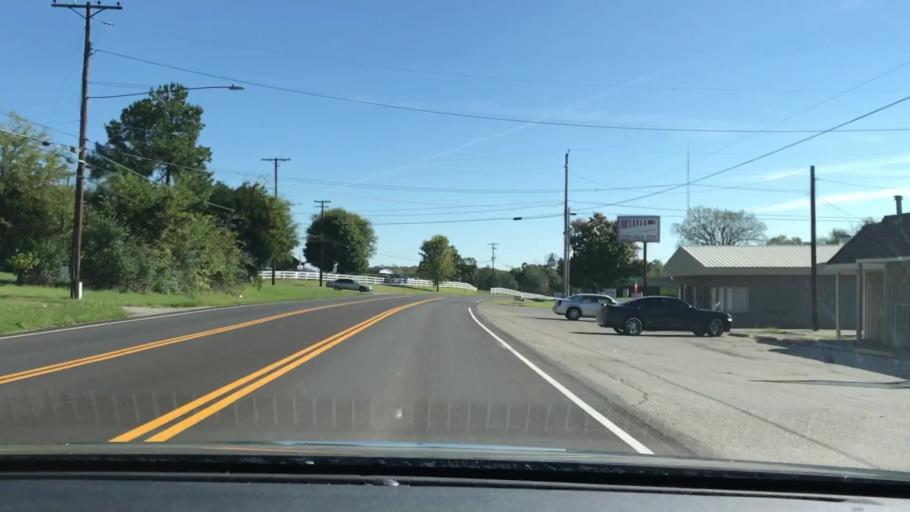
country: US
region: Kentucky
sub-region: Christian County
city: Hopkinsville
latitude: 36.8642
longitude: -87.4591
